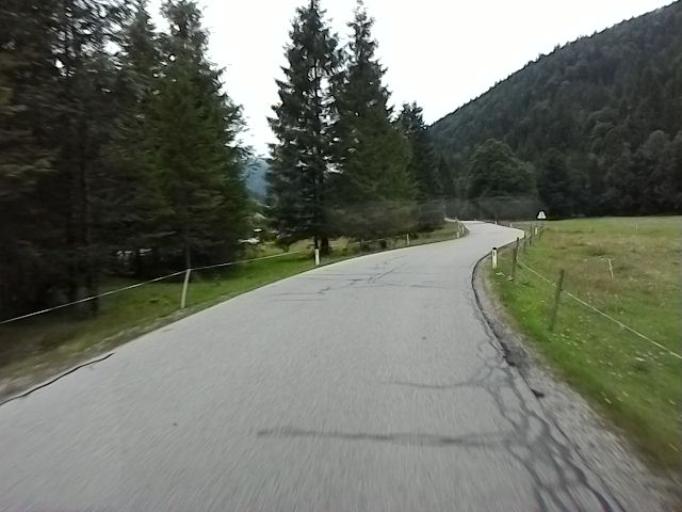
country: DE
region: Bavaria
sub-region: Upper Bavaria
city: Jachenau
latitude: 47.4998
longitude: 11.4572
